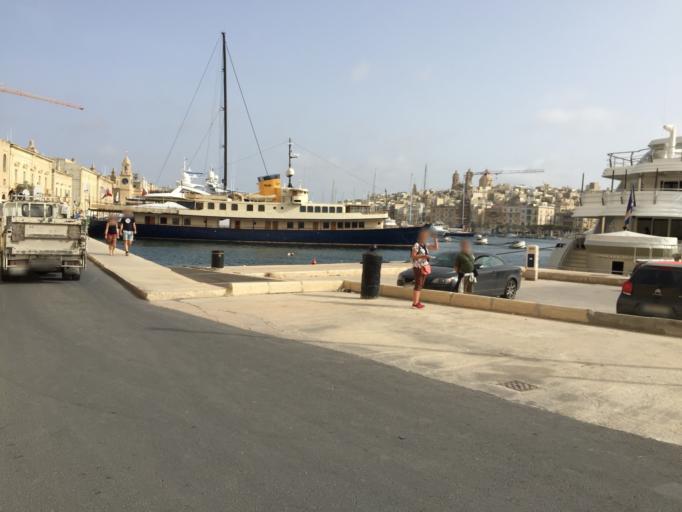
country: MT
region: Il-Birgu
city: Vittoriosa
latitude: 35.8911
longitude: 14.5187
